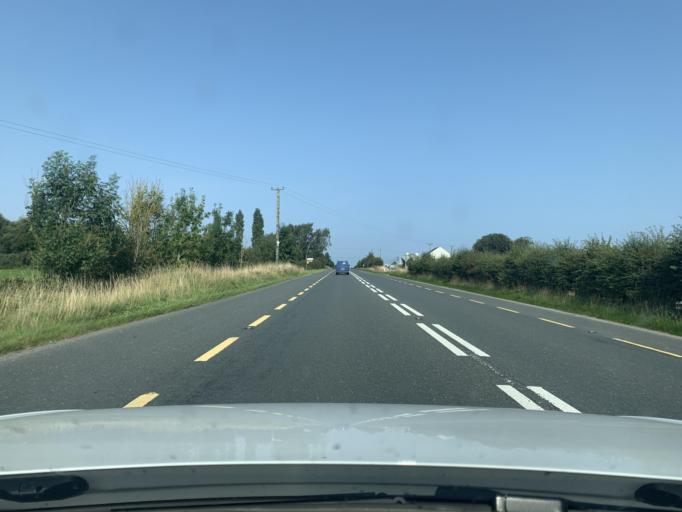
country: IE
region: Leinster
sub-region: An Iarmhi
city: Athlone
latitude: 53.5264
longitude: -8.0592
